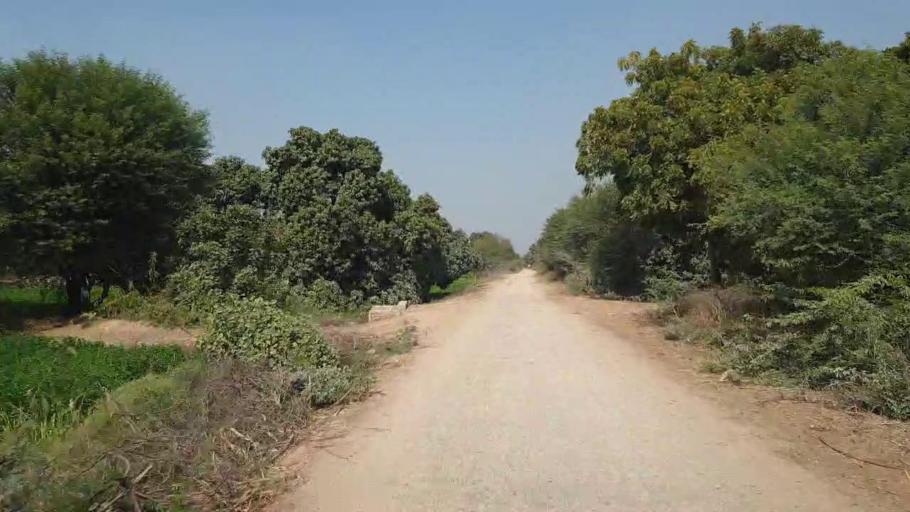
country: PK
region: Sindh
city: Chambar
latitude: 25.4084
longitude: 68.8878
